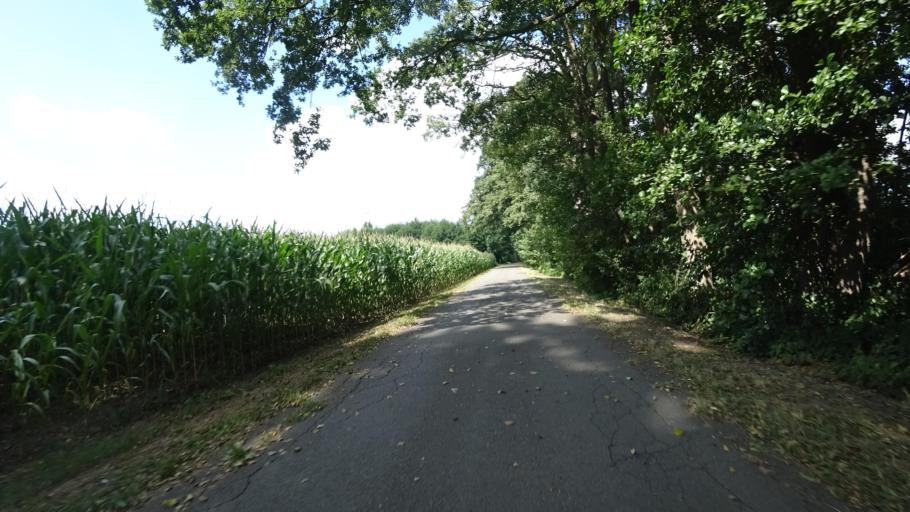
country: DE
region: North Rhine-Westphalia
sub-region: Regierungsbezirk Detmold
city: Guetersloh
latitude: 51.9372
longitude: 8.3770
